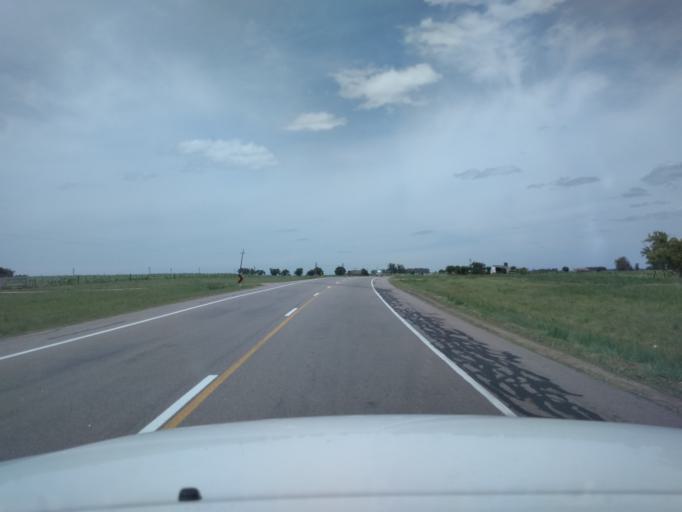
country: UY
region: Florida
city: Cardal
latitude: -34.3172
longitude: -56.2419
